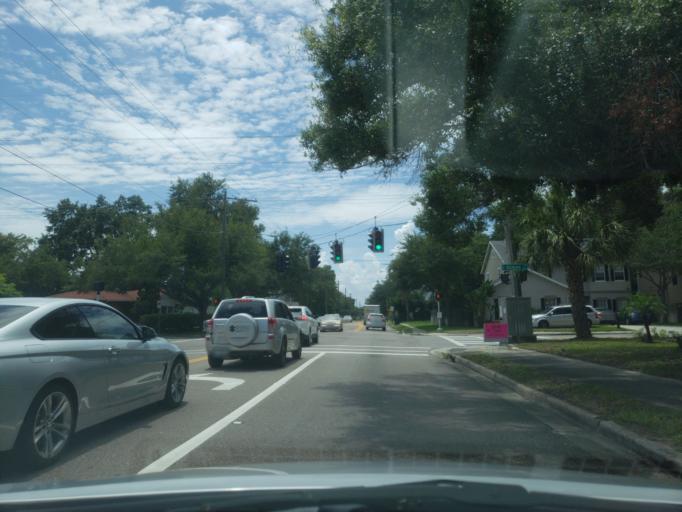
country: US
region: Florida
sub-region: Hillsborough County
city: Tampa
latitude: 27.9087
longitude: -82.5017
